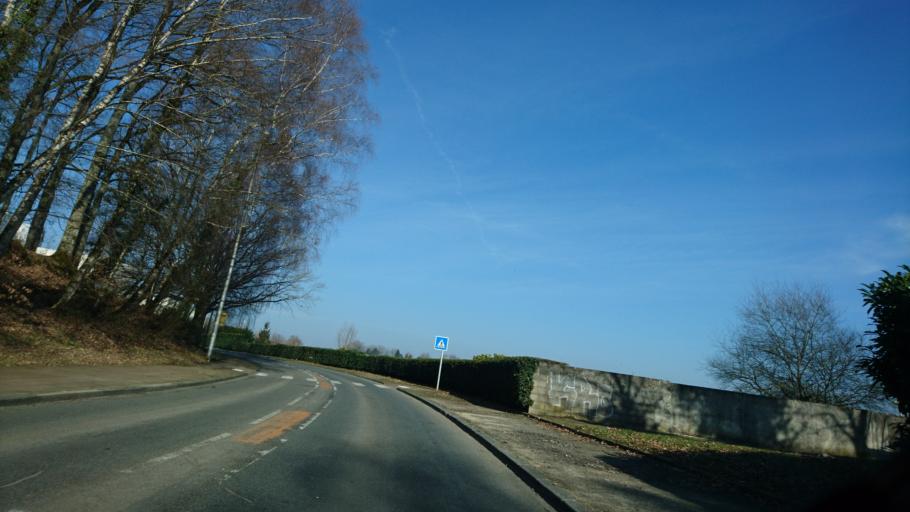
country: FR
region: Limousin
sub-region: Departement de la Haute-Vienne
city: Rilhac-Rancon
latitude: 45.8826
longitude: 1.2986
